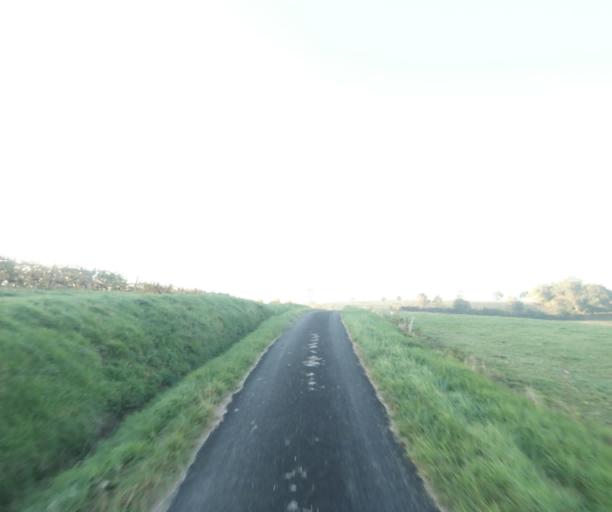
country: FR
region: Midi-Pyrenees
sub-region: Departement du Gers
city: Gondrin
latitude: 43.7828
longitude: 0.1868
